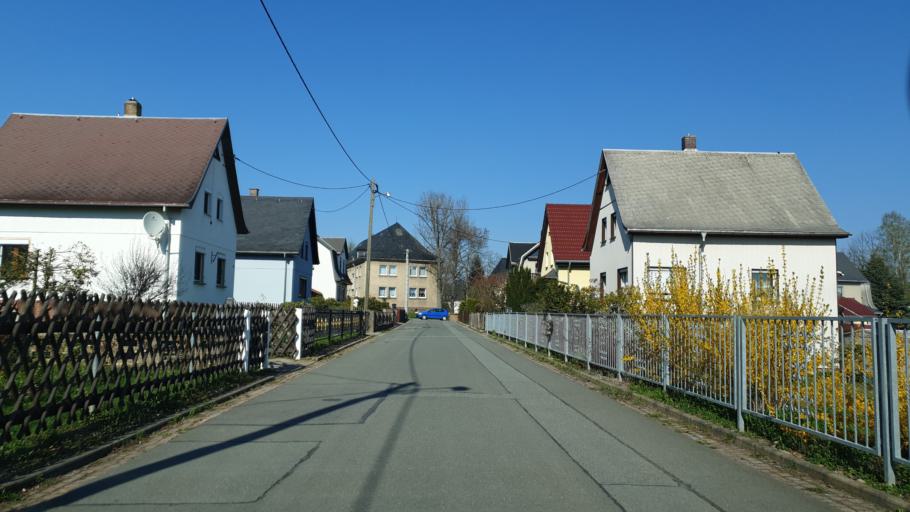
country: DE
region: Saxony
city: Oelsnitz
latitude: 50.7317
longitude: 12.7013
